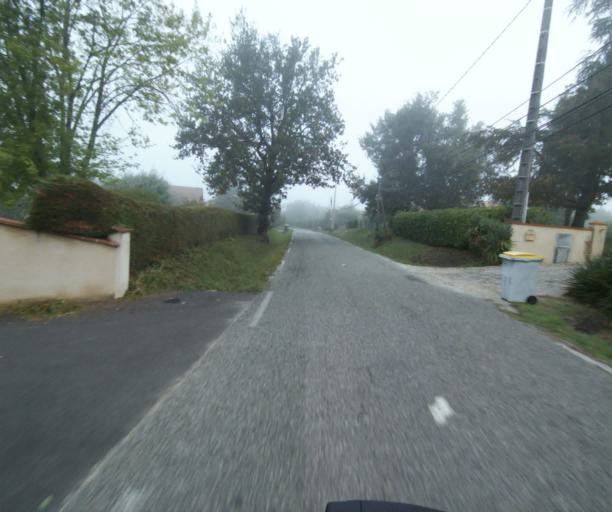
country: FR
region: Midi-Pyrenees
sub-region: Departement du Tarn-et-Garonne
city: Corbarieu
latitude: 43.9524
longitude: 1.3962
